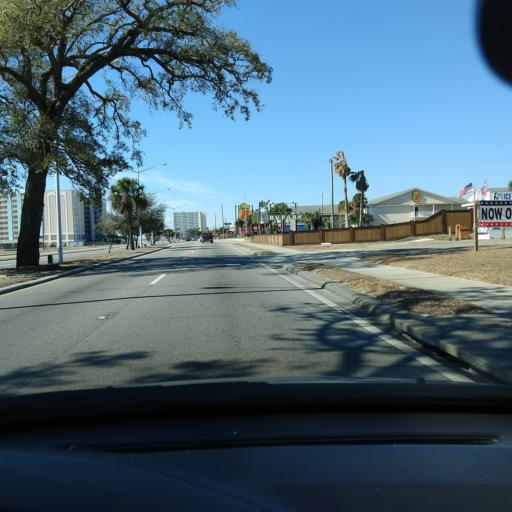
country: US
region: Mississippi
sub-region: Harrison County
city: Biloxi
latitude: 30.3937
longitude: -88.9484
